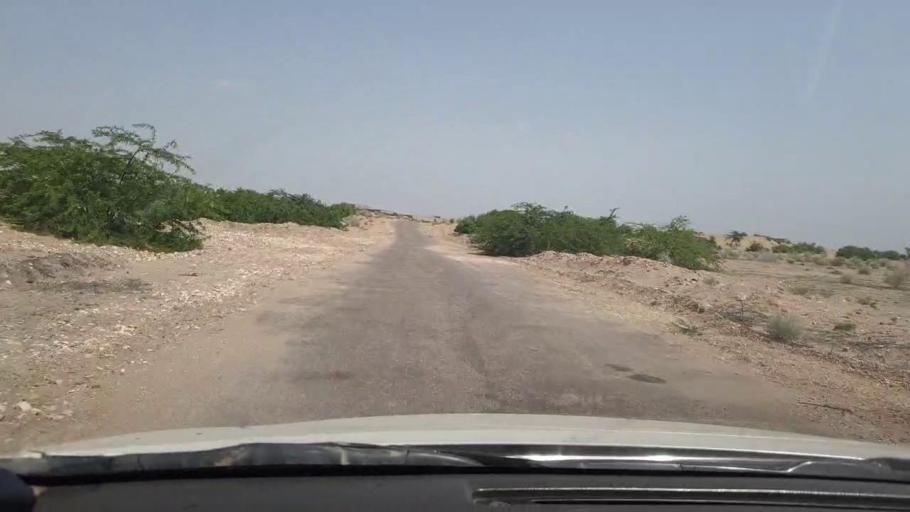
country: PK
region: Sindh
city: Rohri
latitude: 27.4925
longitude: 69.0493
